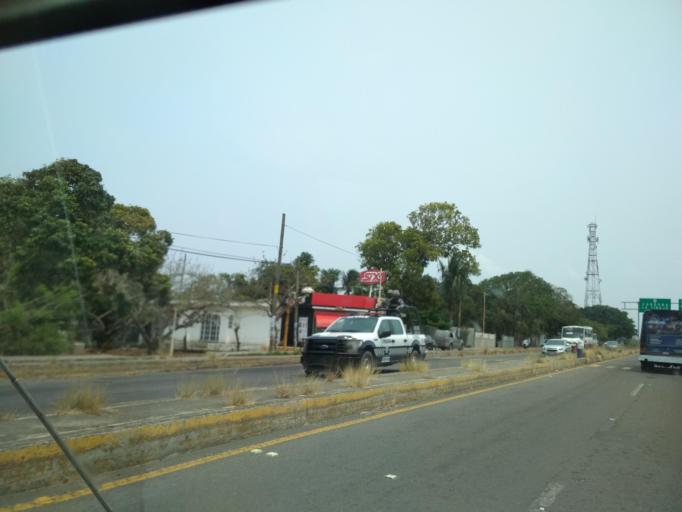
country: MX
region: Veracruz
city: Paso del Toro
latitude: 19.0313
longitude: -96.1378
